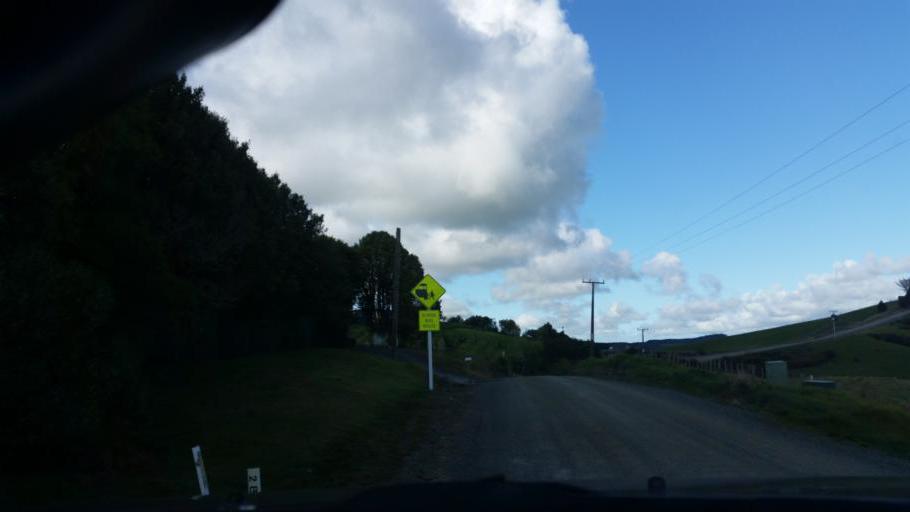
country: NZ
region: Auckland
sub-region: Auckland
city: Wellsford
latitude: -36.1547
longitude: 174.5430
